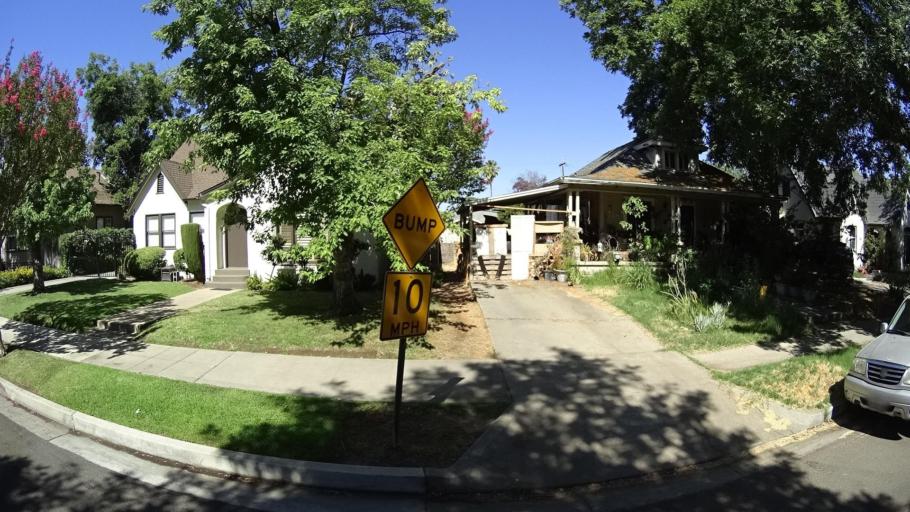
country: US
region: California
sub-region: Fresno County
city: Fresno
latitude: 36.7528
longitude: -119.8041
